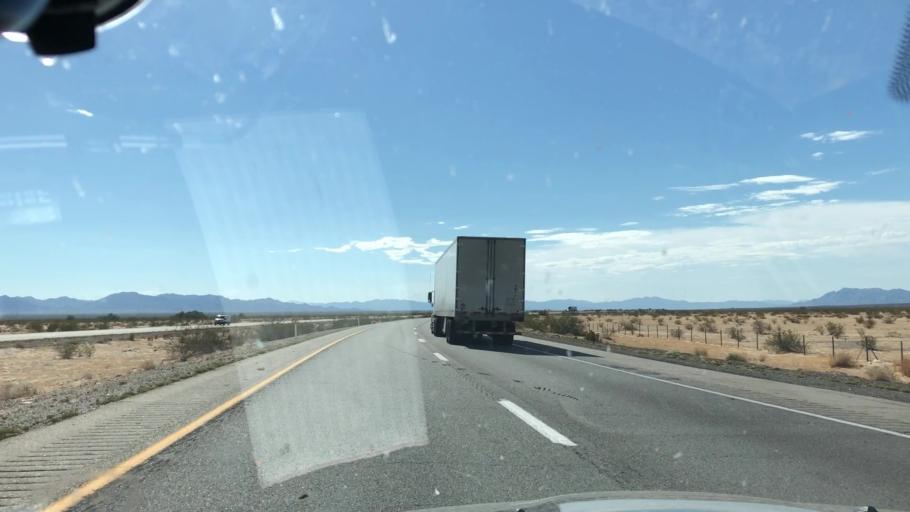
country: US
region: California
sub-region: Riverside County
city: Mesa Verde
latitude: 33.6303
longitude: -115.0721
